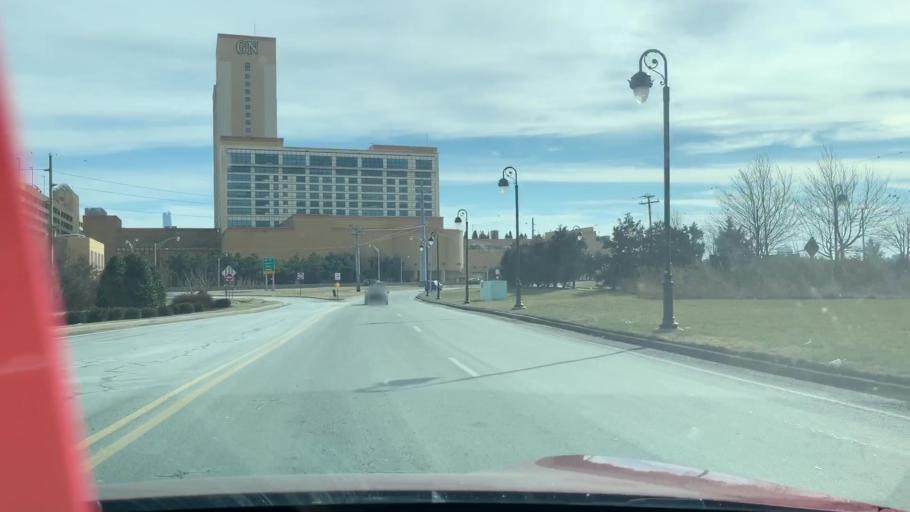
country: US
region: New Jersey
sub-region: Atlantic County
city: Atlantic City
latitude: 39.3823
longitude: -74.4293
